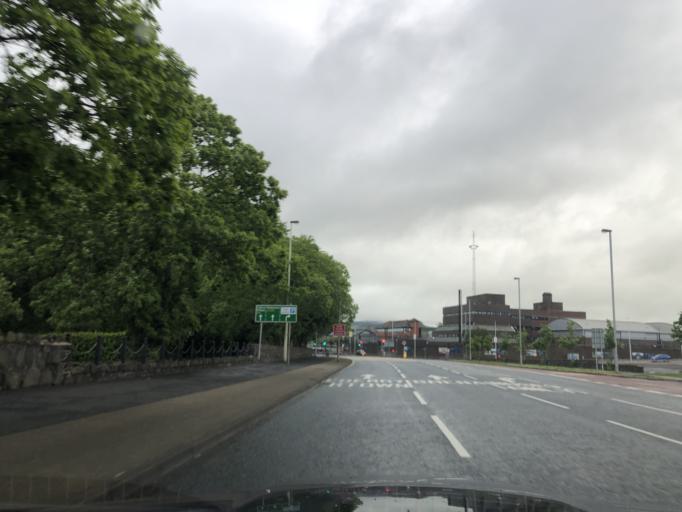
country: GB
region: Northern Ireland
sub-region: Antrim Borough
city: Antrim
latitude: 54.7158
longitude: -6.2220
